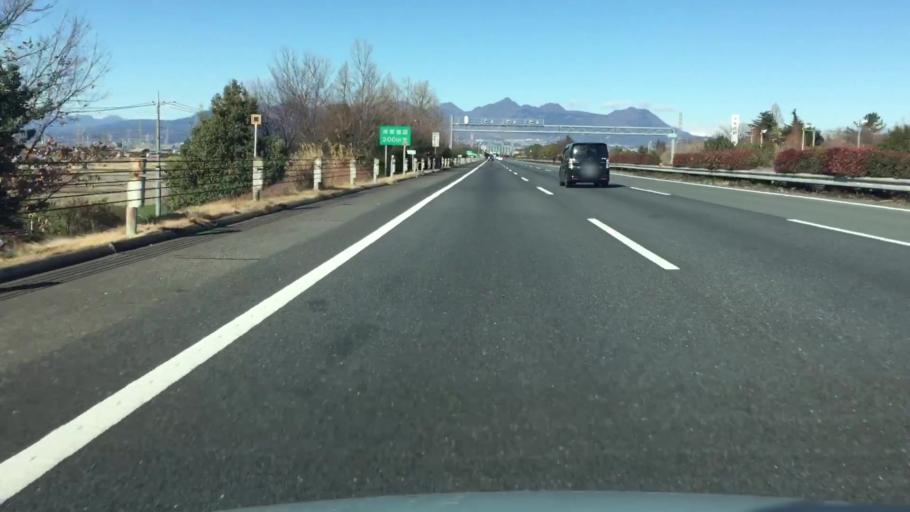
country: JP
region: Gunma
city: Takasaki
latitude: 36.3474
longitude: 139.0505
